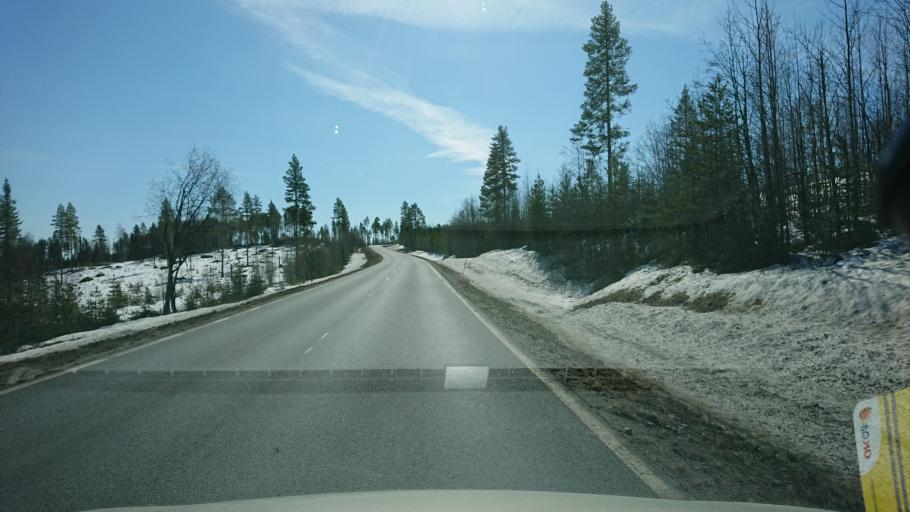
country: SE
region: Vaesterbotten
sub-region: Dorotea Kommun
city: Dorotea
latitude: 64.0221
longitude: 16.2843
